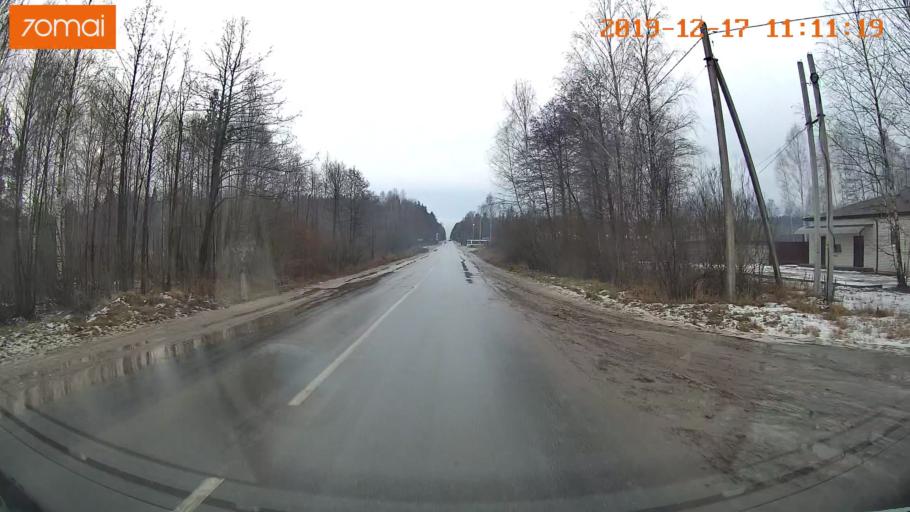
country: RU
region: Vladimir
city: Gus'-Khrustal'nyy
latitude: 55.5875
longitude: 40.6375
